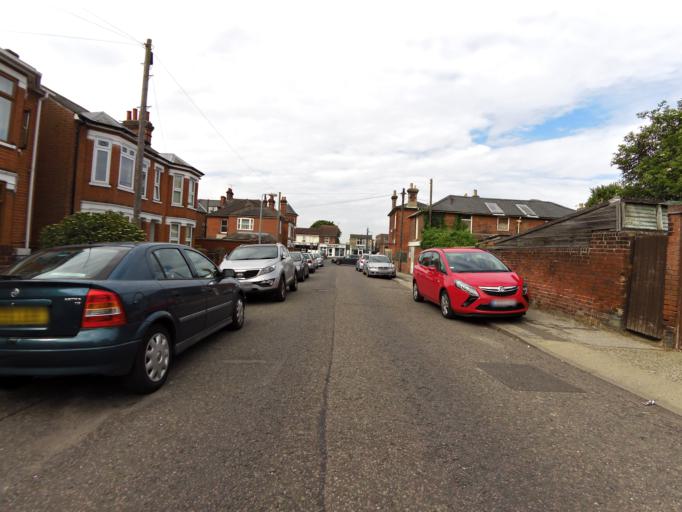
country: GB
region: England
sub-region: Suffolk
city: Ipswich
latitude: 52.0678
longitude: 1.1383
